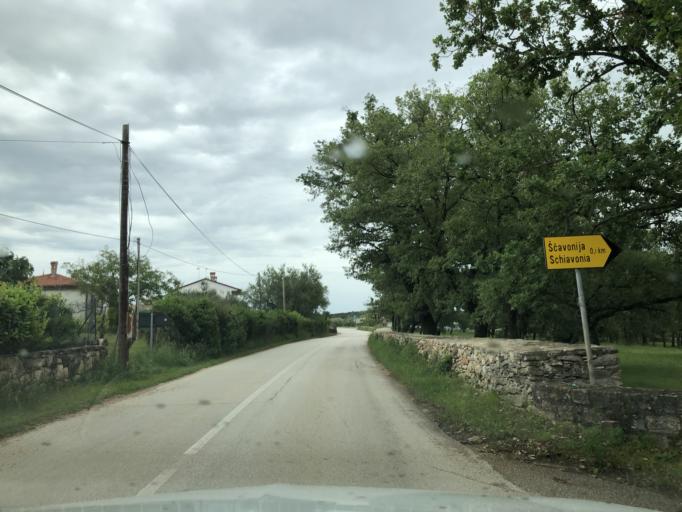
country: HR
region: Istarska
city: Buje
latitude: 45.4439
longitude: 13.6475
